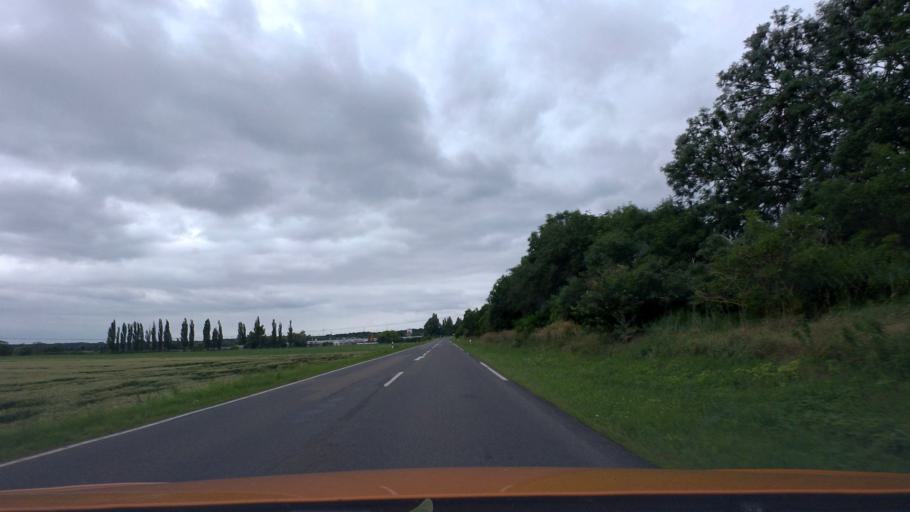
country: DE
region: Brandenburg
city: Wriezen
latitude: 52.7209
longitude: 14.1550
